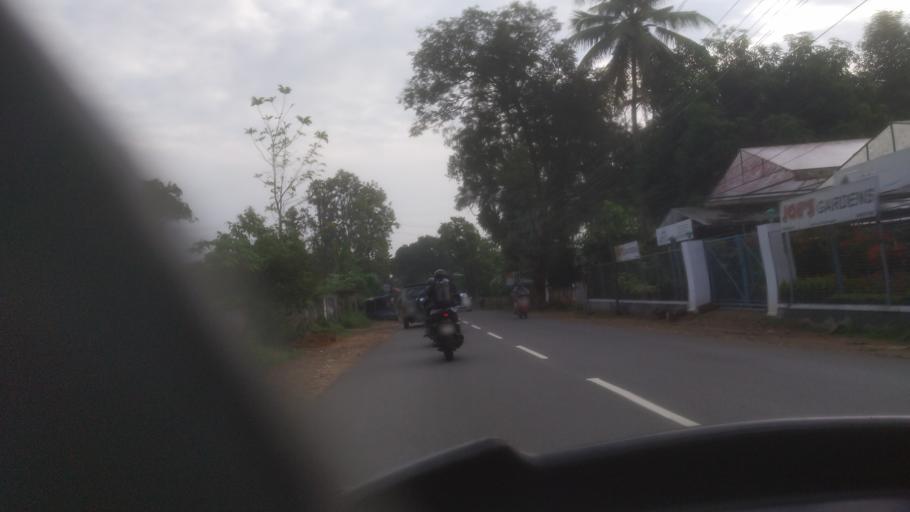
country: IN
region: Kerala
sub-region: Ernakulam
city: Kotamangalam
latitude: 10.0592
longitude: 76.6396
